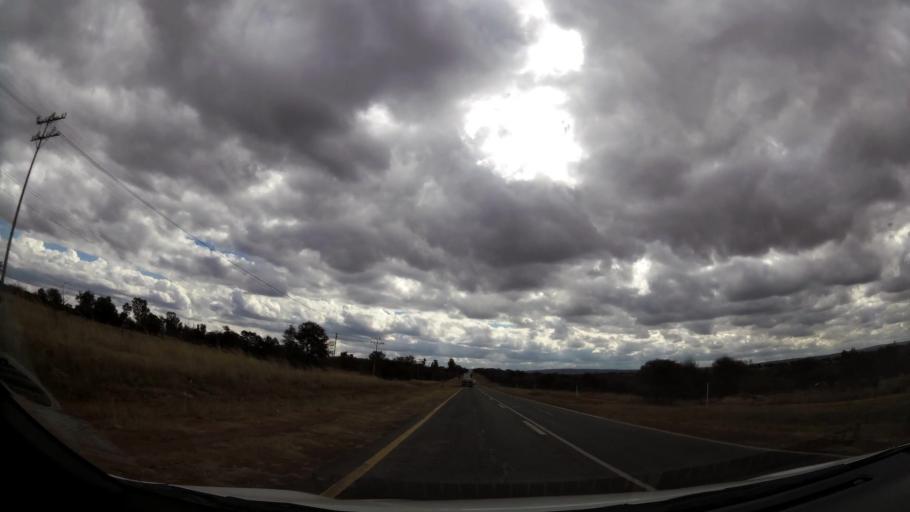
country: ZA
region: Limpopo
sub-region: Waterberg District Municipality
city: Modimolle
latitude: -24.7395
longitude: 28.4371
